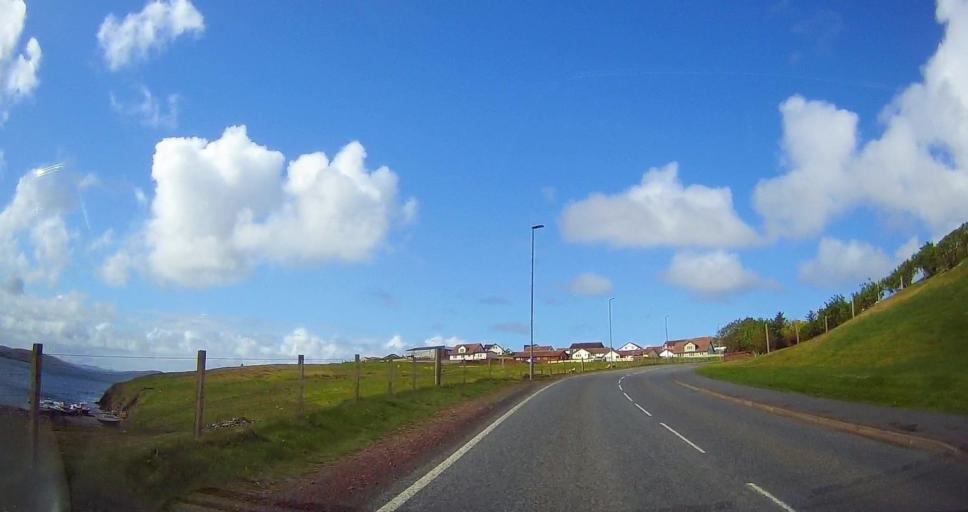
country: GB
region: Scotland
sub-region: Shetland Islands
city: Lerwick
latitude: 60.3925
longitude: -1.3670
